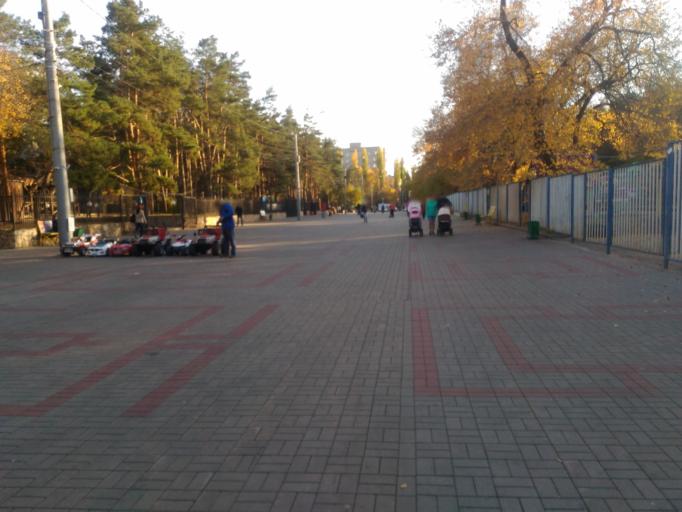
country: RU
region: Voronezj
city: Voronezh
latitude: 51.6534
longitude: 39.1283
